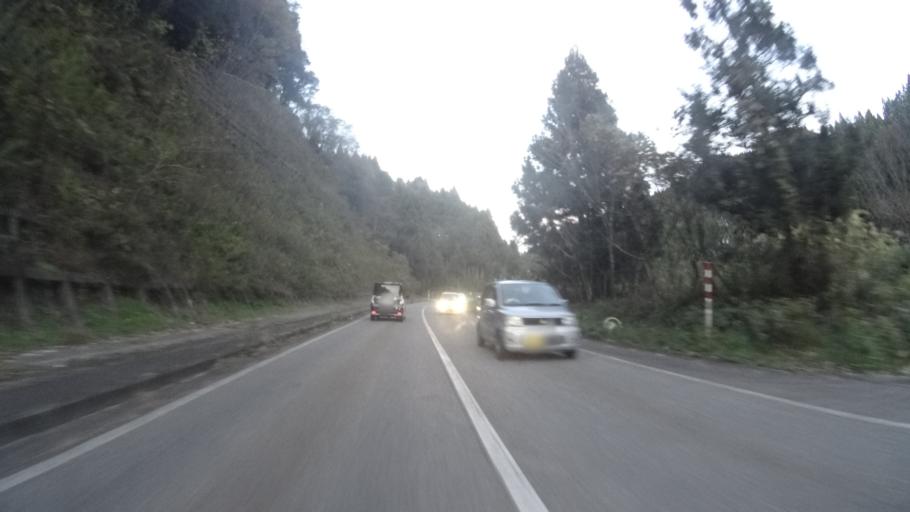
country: JP
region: Ishikawa
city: Nanao
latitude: 37.3173
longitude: 136.8060
